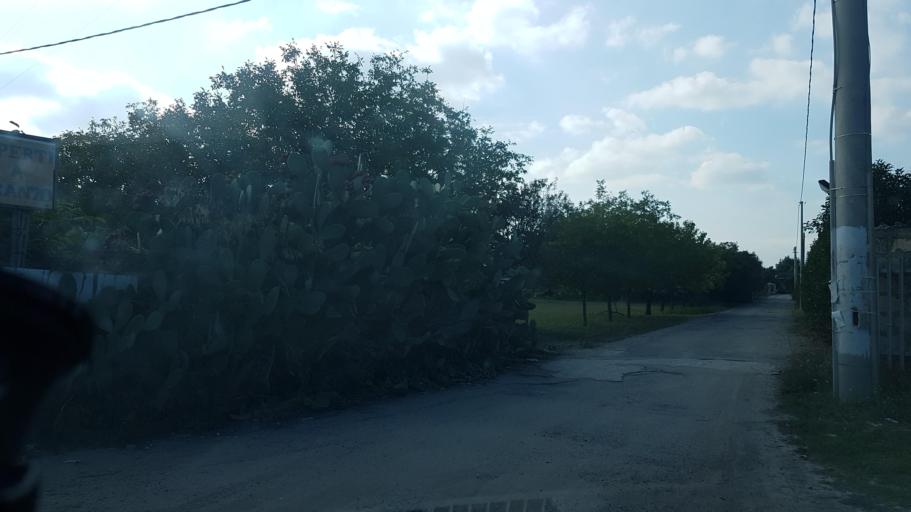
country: IT
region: Apulia
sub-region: Provincia di Foggia
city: Foggia
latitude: 41.4413
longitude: 15.5243
